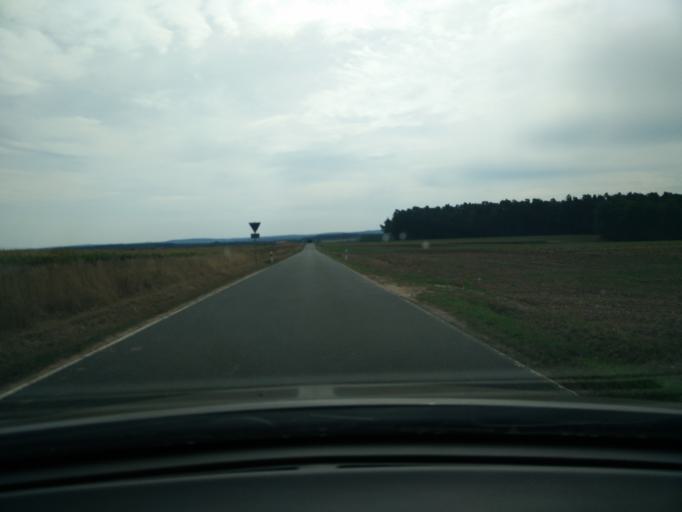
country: DE
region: Bavaria
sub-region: Regierungsbezirk Mittelfranken
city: Puschendorf
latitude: 49.5326
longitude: 10.8026
